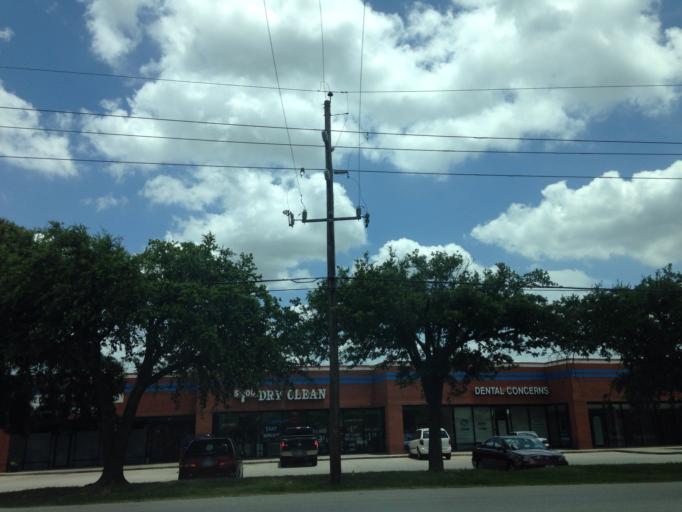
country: US
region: Texas
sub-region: Harris County
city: Spring
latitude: 30.0422
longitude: -95.4895
